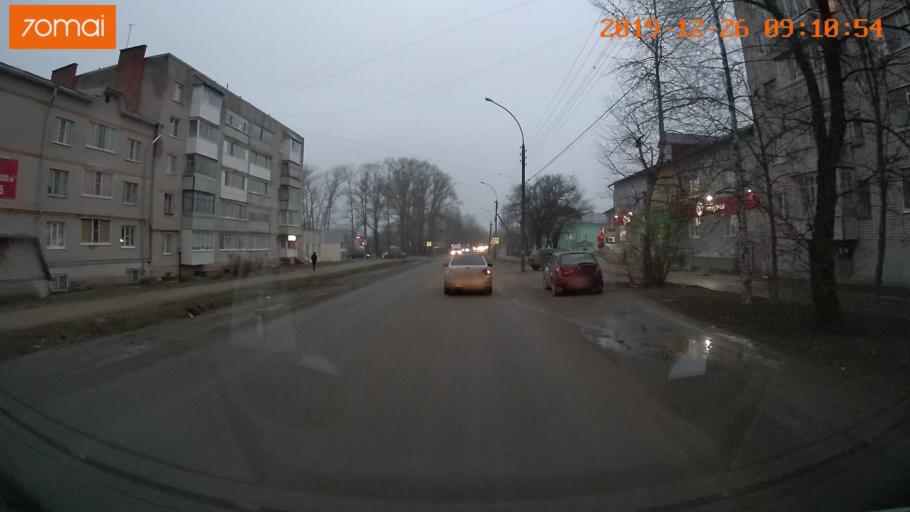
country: RU
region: Vologda
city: Gryazovets
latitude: 58.8734
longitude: 40.2525
